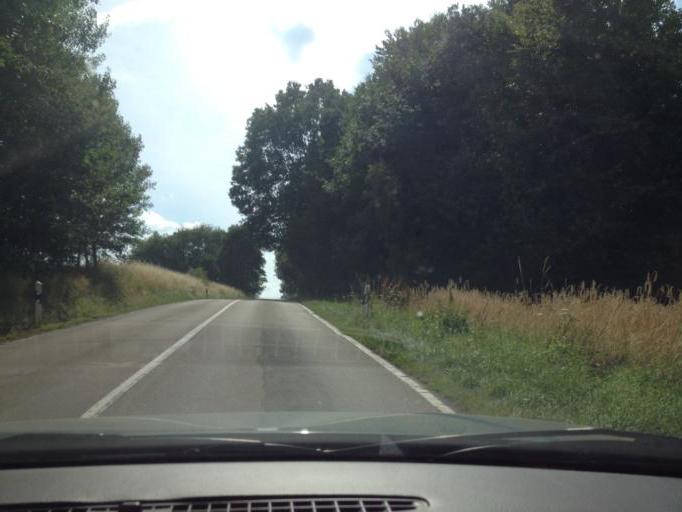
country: DE
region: Saarland
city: Ottweiler
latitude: 49.3976
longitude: 7.1390
